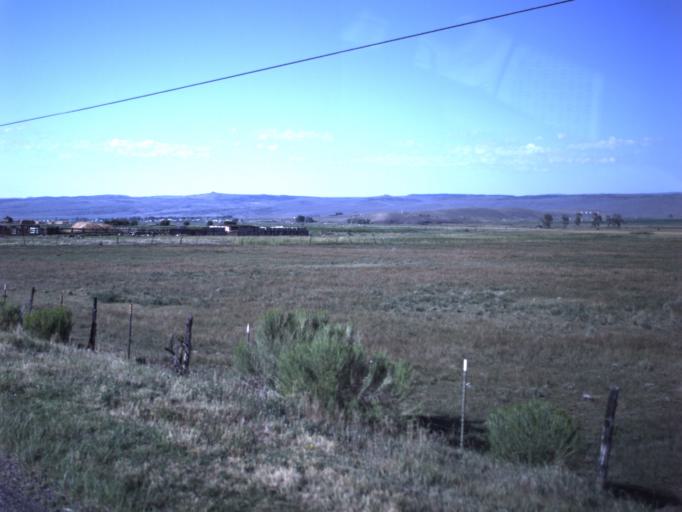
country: US
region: Utah
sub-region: Wayne County
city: Loa
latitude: 38.4488
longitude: -111.6158
